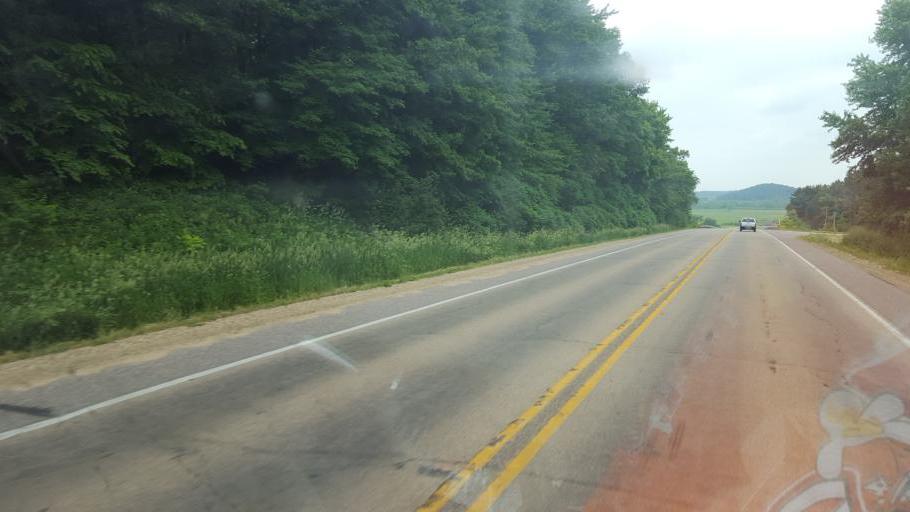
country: US
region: Wisconsin
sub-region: Sauk County
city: Reedsburg
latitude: 43.6018
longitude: -90.1339
